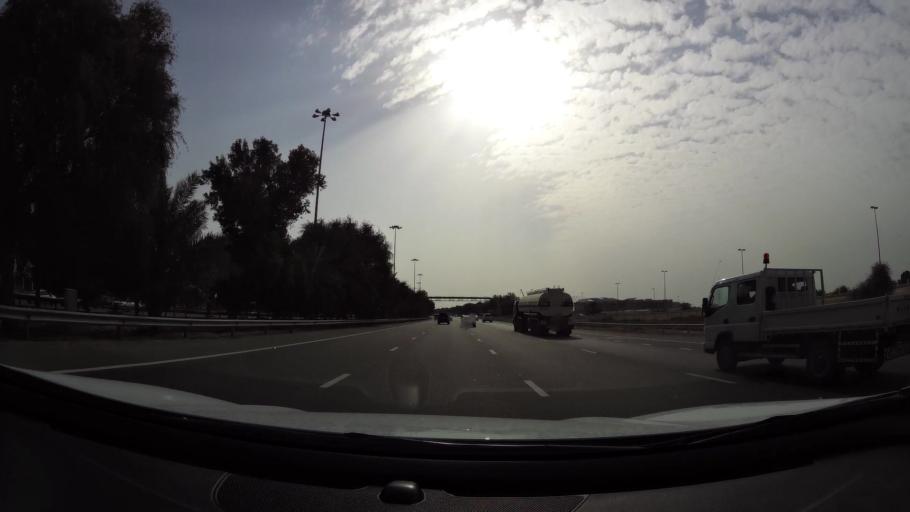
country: AE
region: Abu Dhabi
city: Abu Dhabi
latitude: 24.3192
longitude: 54.6108
